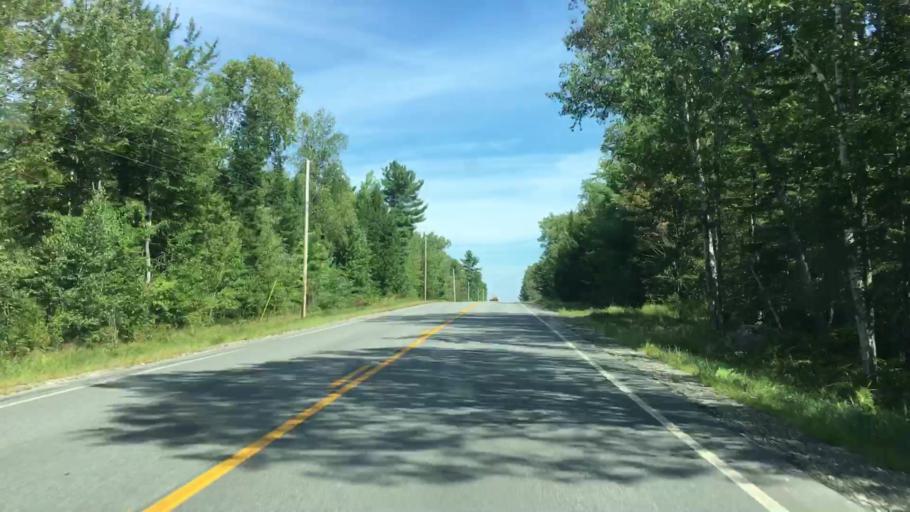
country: US
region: Maine
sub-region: Penobscot County
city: Howland
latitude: 45.2337
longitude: -68.6891
